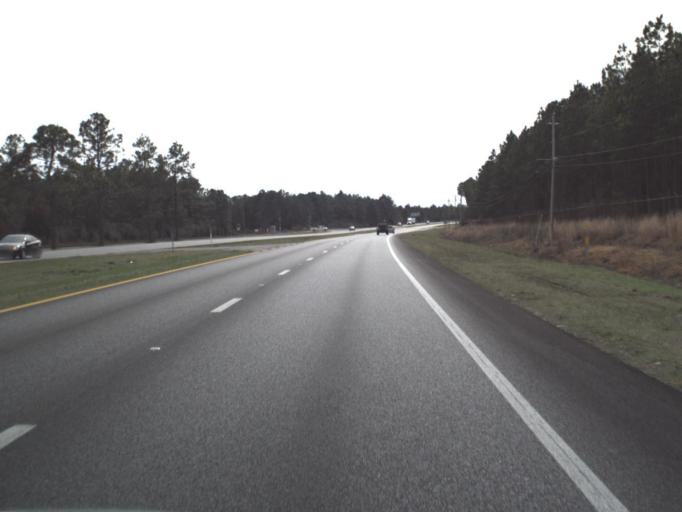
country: US
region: Florida
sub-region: Bay County
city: Youngstown
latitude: 30.3379
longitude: -85.4423
